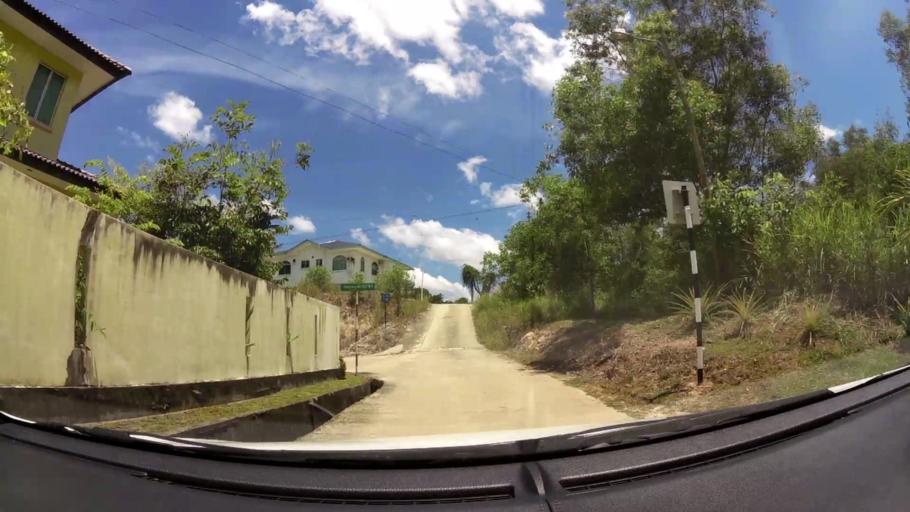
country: BN
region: Brunei and Muara
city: Bandar Seri Begawan
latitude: 4.9374
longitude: 114.9657
